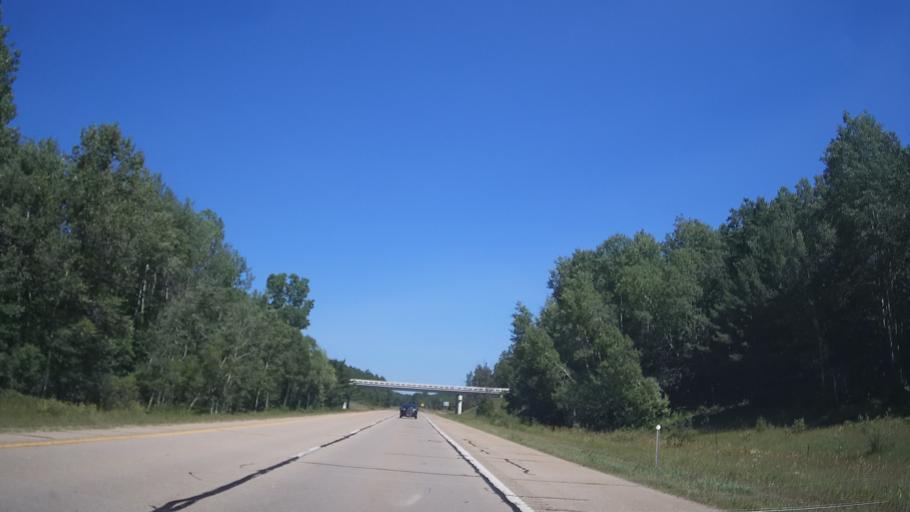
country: US
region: Michigan
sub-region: Clare County
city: Clare
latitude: 43.8696
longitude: -84.8657
